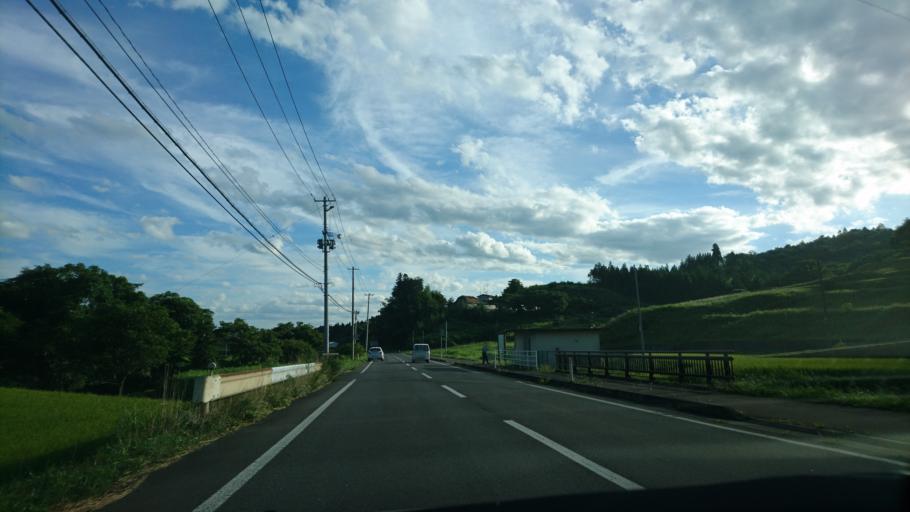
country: JP
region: Iwate
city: Ichinoseki
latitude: 38.8654
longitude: 141.1870
